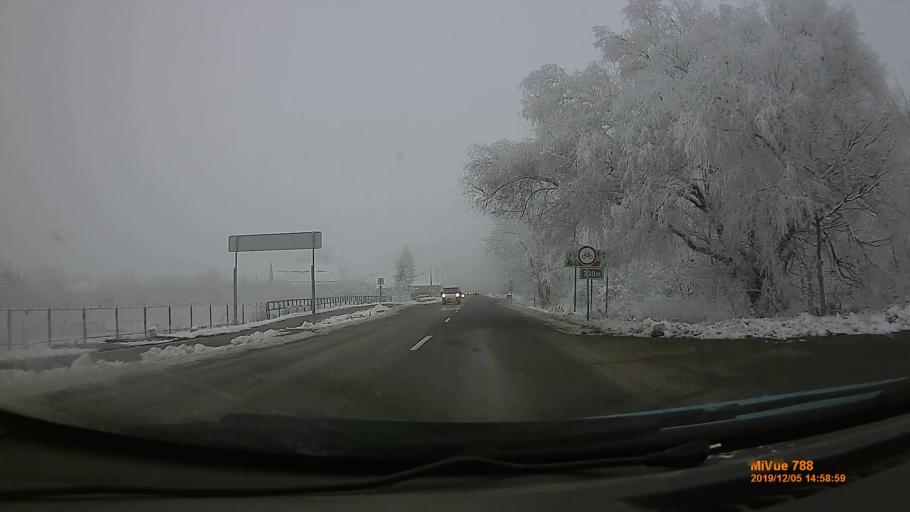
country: HU
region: Szabolcs-Szatmar-Bereg
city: Nyirtelek
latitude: 48.0535
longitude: 21.5634
